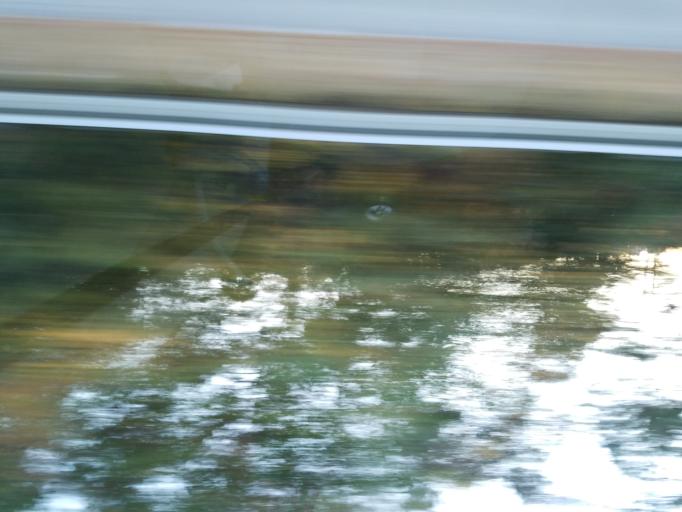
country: US
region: Georgia
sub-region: Forsyth County
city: Cumming
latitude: 34.2576
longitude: -84.0912
